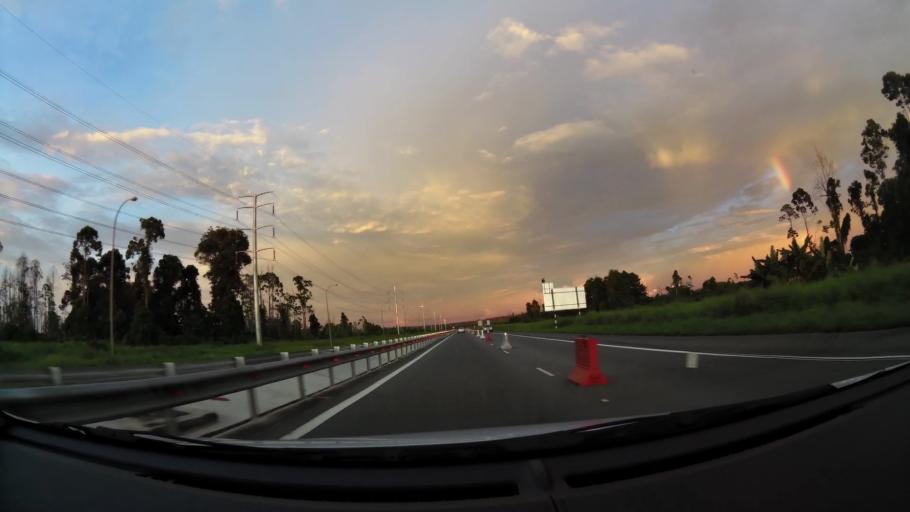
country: BN
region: Belait
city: Kuala Belait
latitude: 4.5789
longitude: 114.2675
